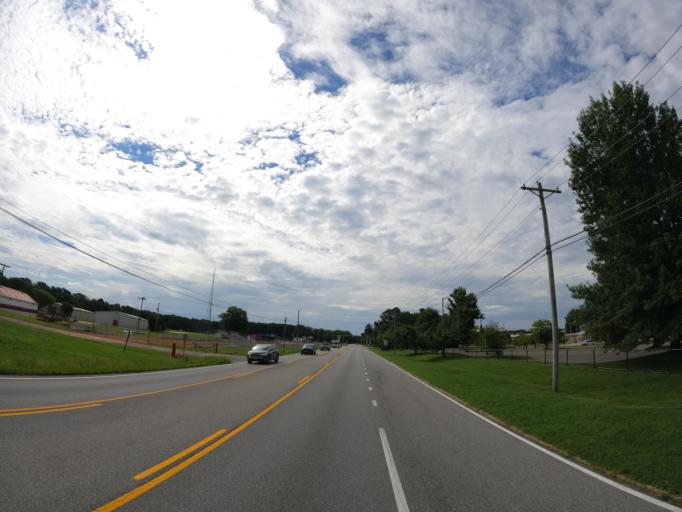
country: US
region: Maryland
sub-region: Saint Mary's County
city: Leonardtown
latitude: 38.2729
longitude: -76.6102
